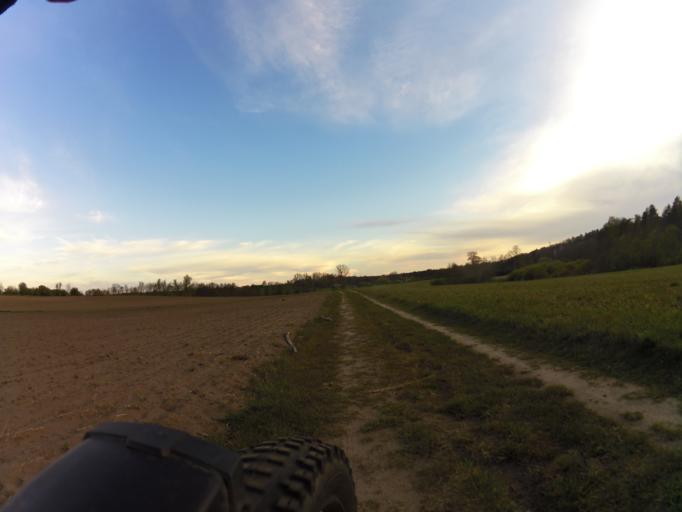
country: PL
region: West Pomeranian Voivodeship
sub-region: Powiat lobeski
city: Lobez
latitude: 53.7084
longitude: 15.6496
